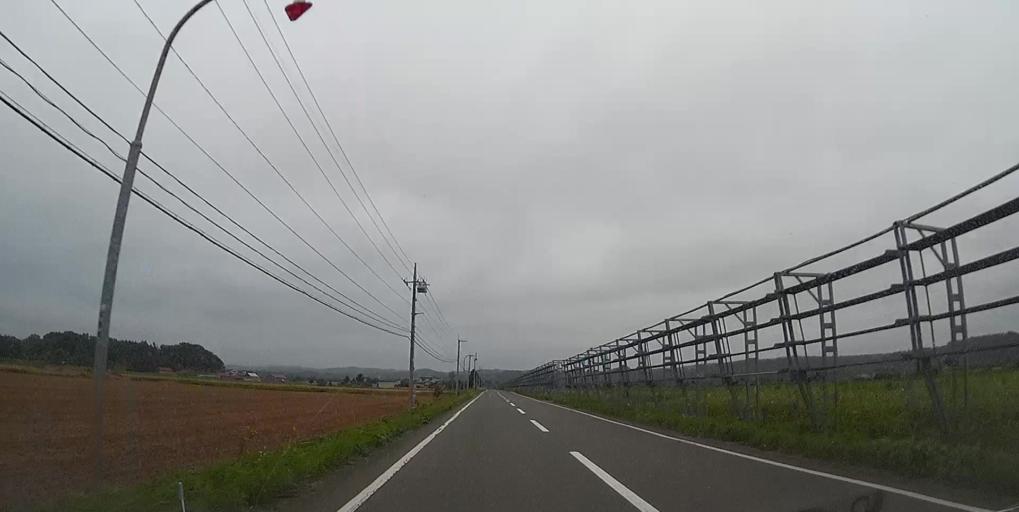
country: JP
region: Hokkaido
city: Iwanai
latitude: 42.4024
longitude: 140.0049
